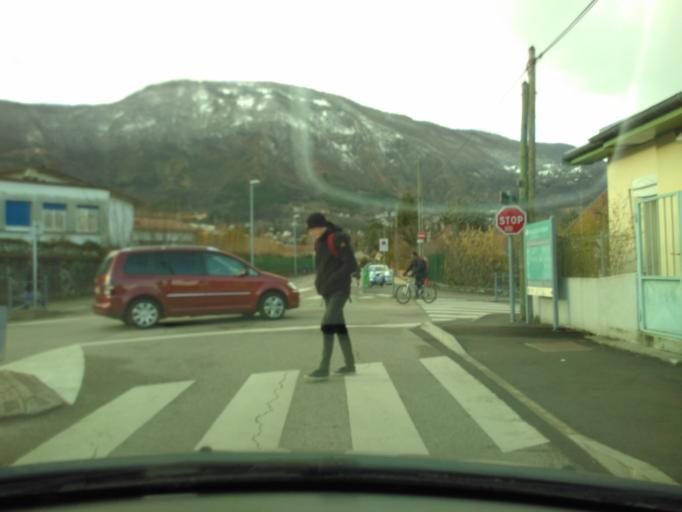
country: FR
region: Rhone-Alpes
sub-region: Departement de l'Isere
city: La Tronche
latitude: 45.1998
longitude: 5.7503
